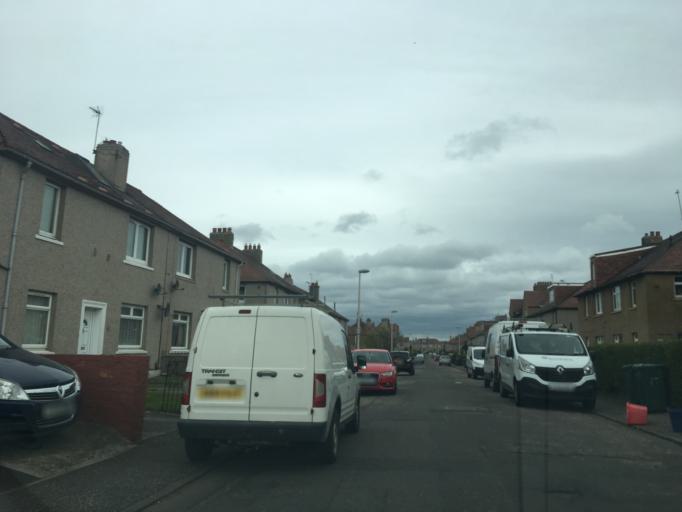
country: GB
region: Scotland
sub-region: Edinburgh
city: Colinton
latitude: 55.9241
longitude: -3.2758
